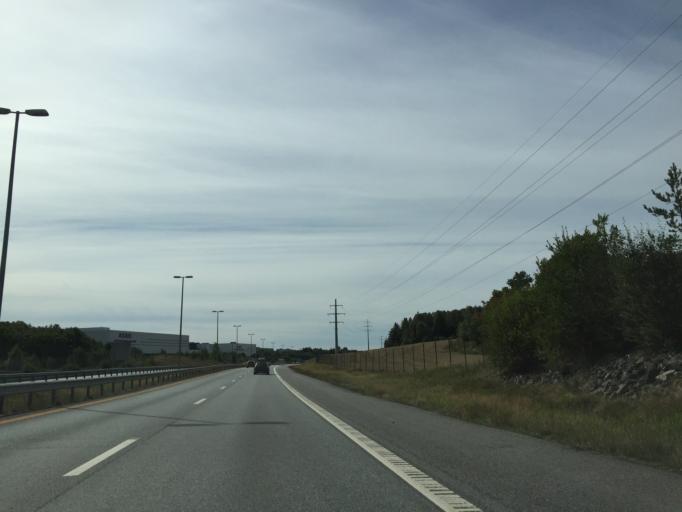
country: NO
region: Akershus
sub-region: Vestby
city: Vestby
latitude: 59.5959
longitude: 10.7388
